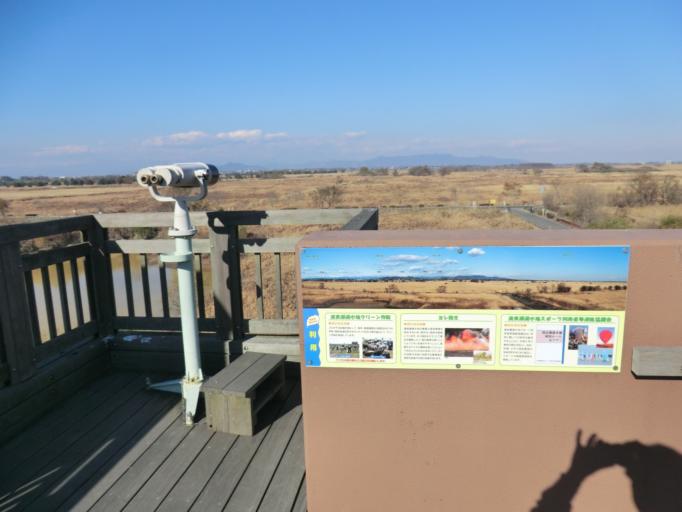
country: JP
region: Tochigi
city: Fujioka
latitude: 36.2313
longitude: 139.6693
